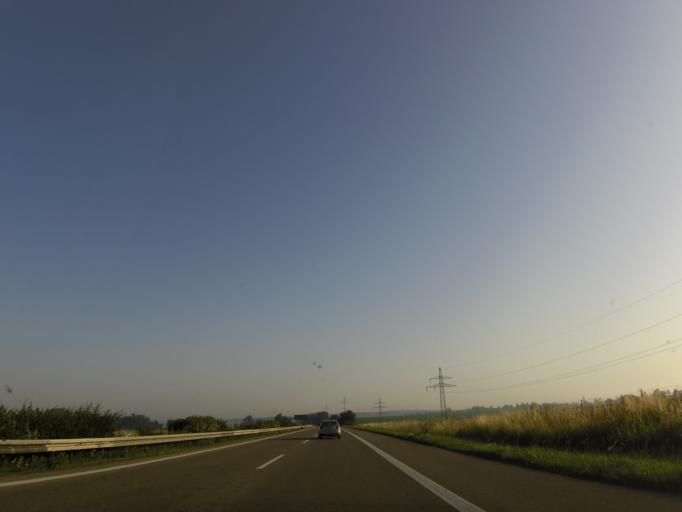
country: DE
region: Bavaria
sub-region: Swabia
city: Senden
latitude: 48.3348
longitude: 10.0882
